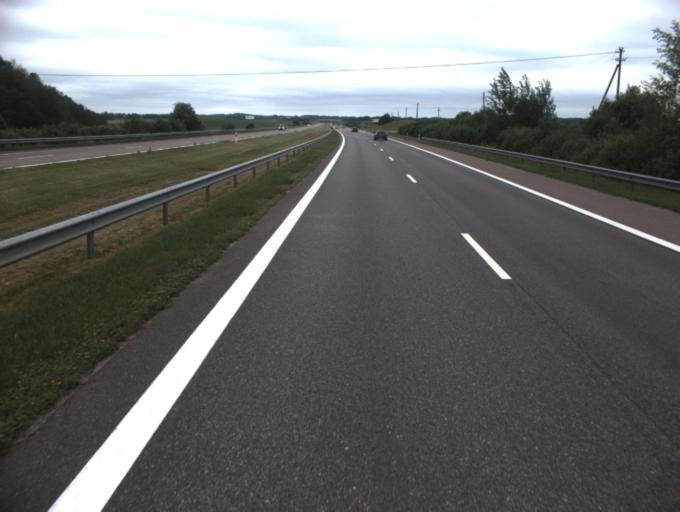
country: LT
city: Skaudvile
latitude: 55.4692
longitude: 22.6669
